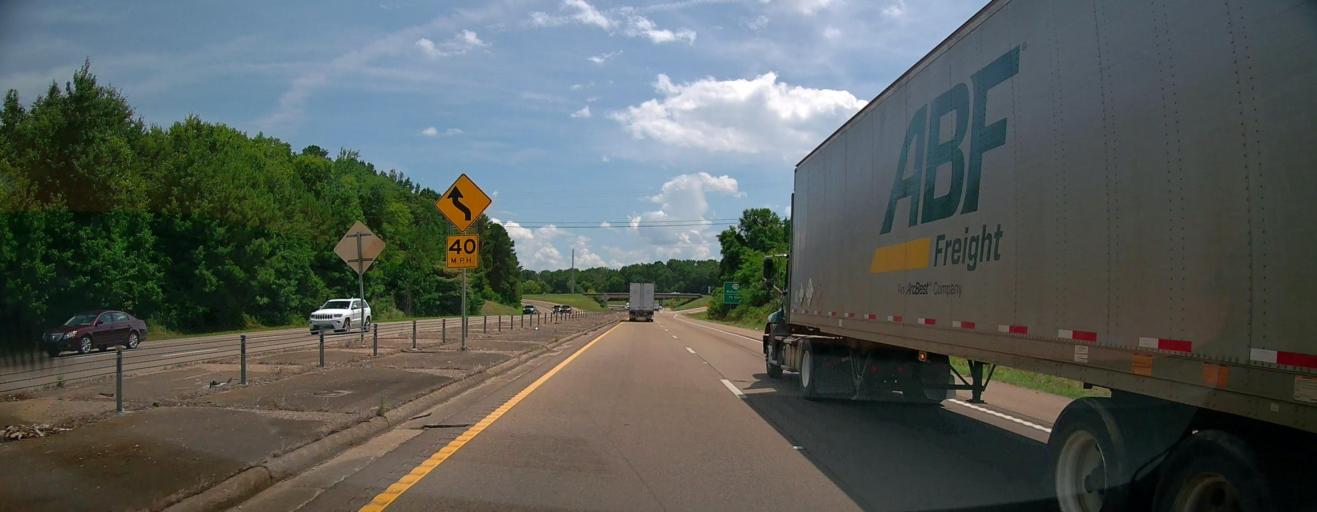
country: US
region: Mississippi
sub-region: Lee County
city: Tupelo
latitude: 34.2791
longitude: -88.7075
